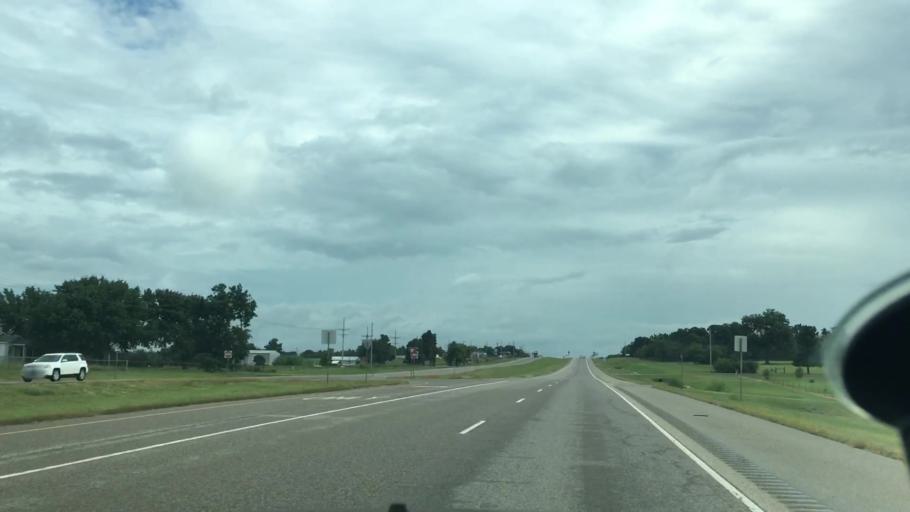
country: US
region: Oklahoma
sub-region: Seminole County
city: Seminole
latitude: 35.3556
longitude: -96.6718
